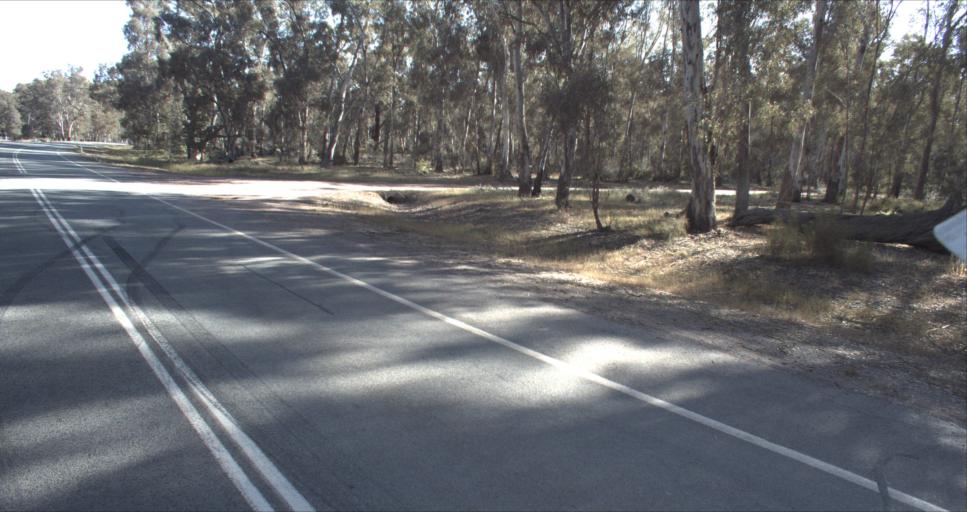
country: AU
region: New South Wales
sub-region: Leeton
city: Leeton
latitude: -34.6353
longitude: 146.3756
